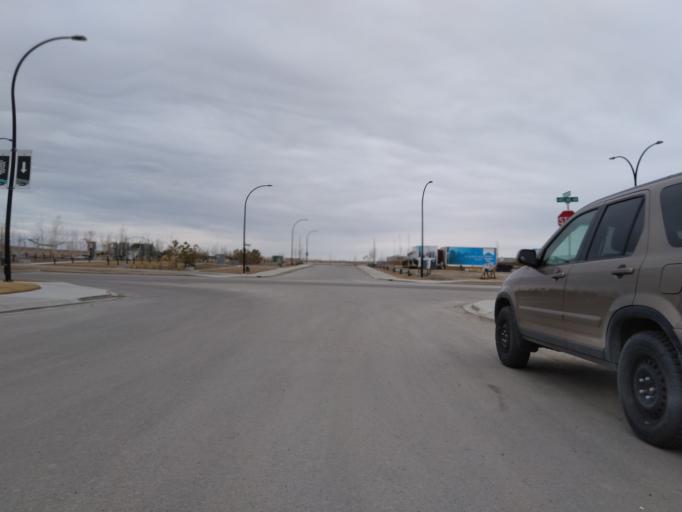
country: CA
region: Alberta
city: Calgary
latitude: 51.1811
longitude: -114.0918
